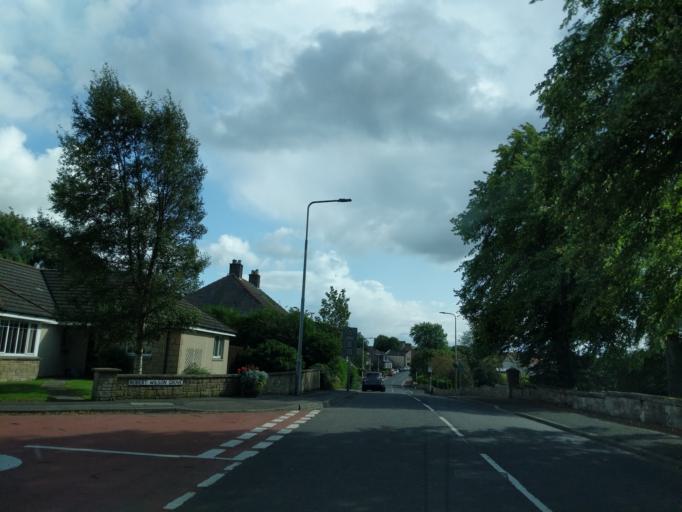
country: GB
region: Scotland
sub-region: Fife
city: Townhill
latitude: 56.0920
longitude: -3.4403
